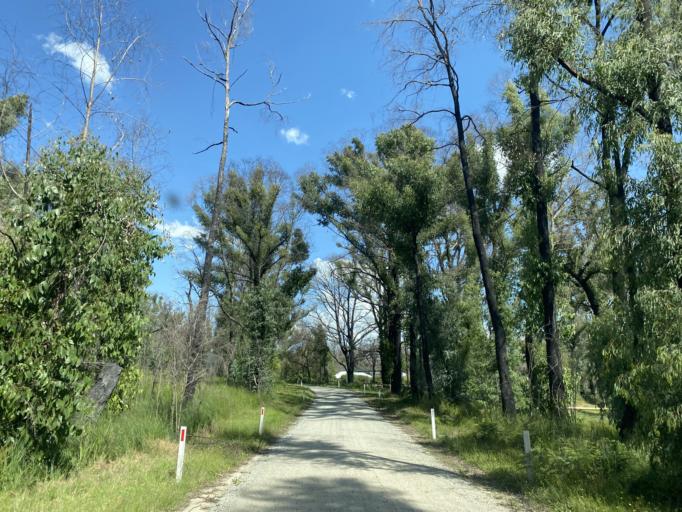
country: AU
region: Victoria
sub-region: Cardinia
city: Bunyip
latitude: -38.0034
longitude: 145.7378
